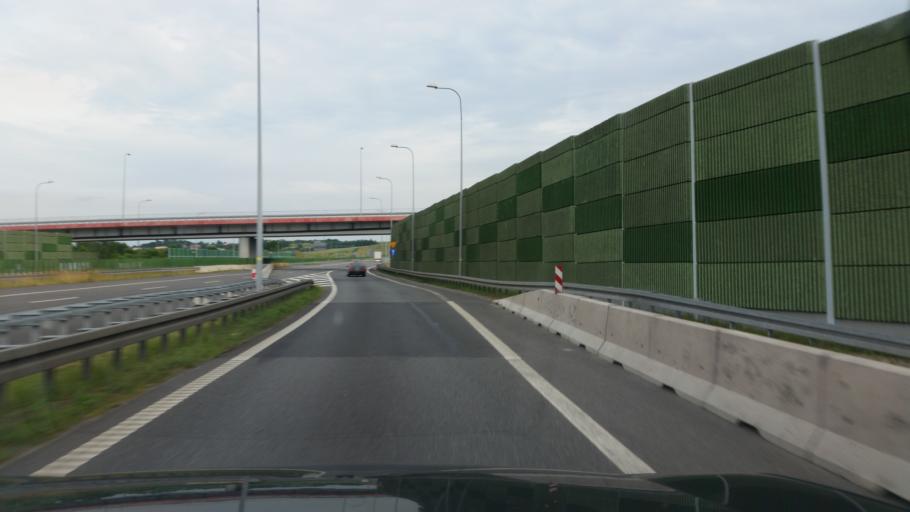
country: PL
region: Silesian Voivodeship
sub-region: Powiat tarnogorski
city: Ozarowice
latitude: 50.4495
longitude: 19.0558
